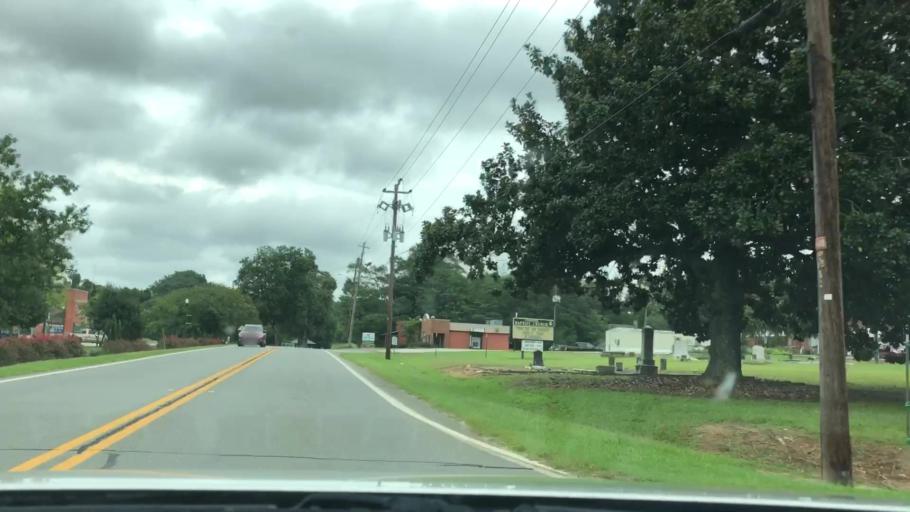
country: US
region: Georgia
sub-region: Pike County
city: Zebulon
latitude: 33.0907
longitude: -84.4397
